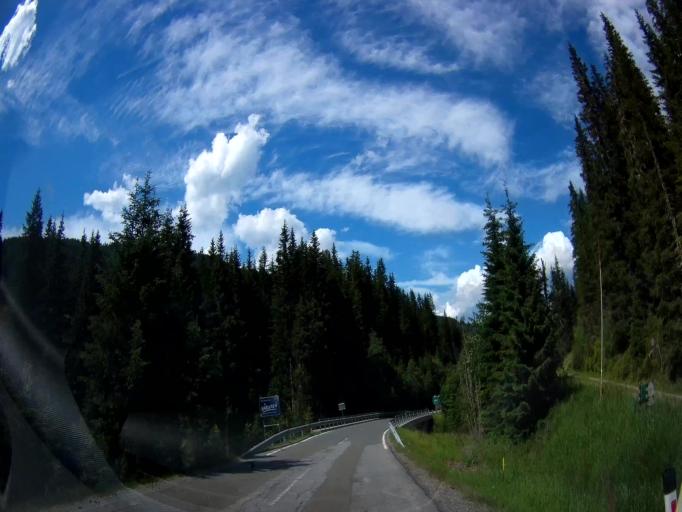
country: AT
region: Styria
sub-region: Politischer Bezirk Murau
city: Stadl an der Mur
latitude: 46.9781
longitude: 14.0063
